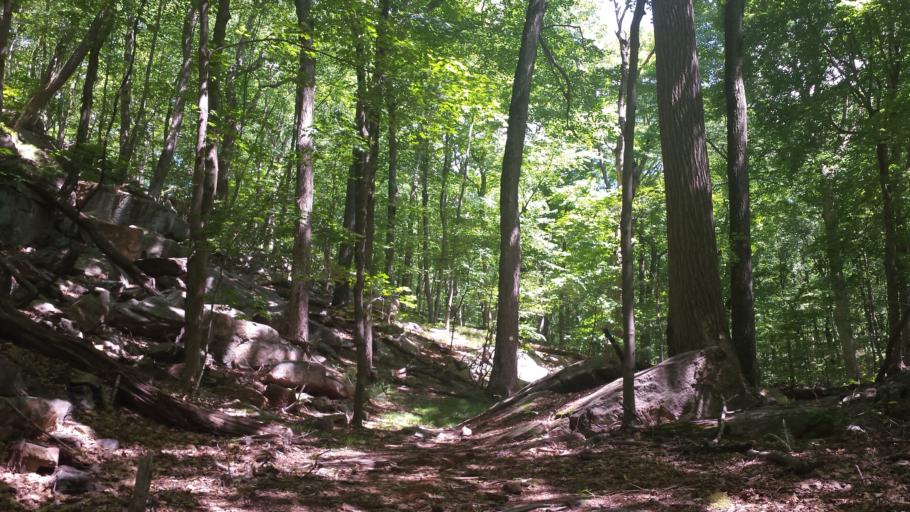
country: US
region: New York
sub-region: Westchester County
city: Pound Ridge
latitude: 41.2504
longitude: -73.5782
